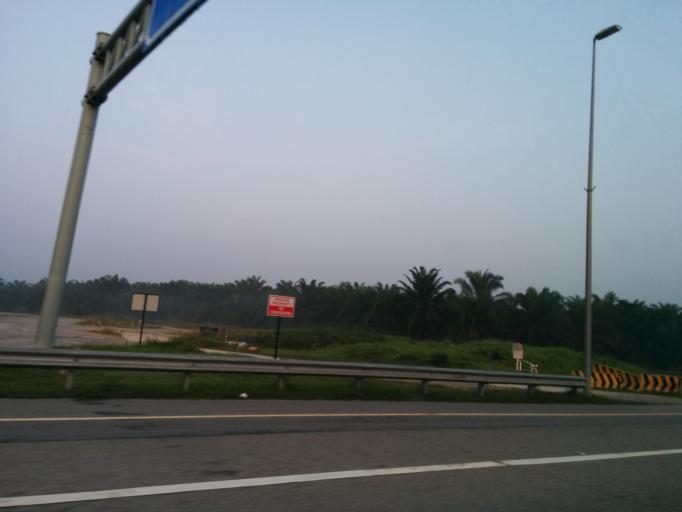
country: MY
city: Sungai Pelek New Village
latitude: 2.7582
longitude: 101.6875
